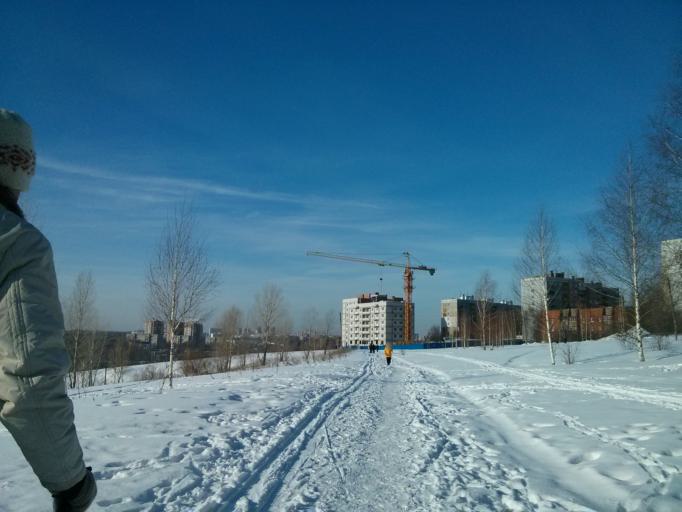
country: RU
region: Nizjnij Novgorod
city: Afonino
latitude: 56.2913
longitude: 44.0641
